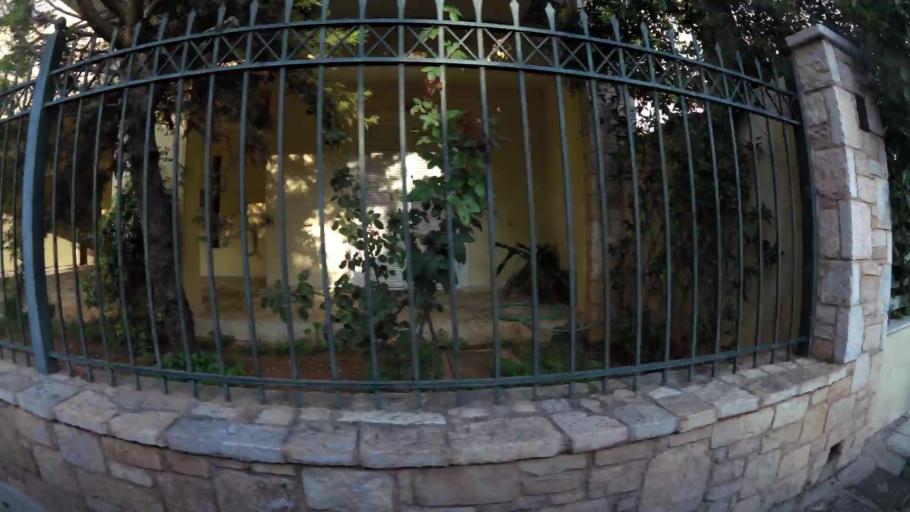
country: GR
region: Attica
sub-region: Nomarchia Anatolikis Attikis
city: Acharnes
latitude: 38.0810
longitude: 23.7339
